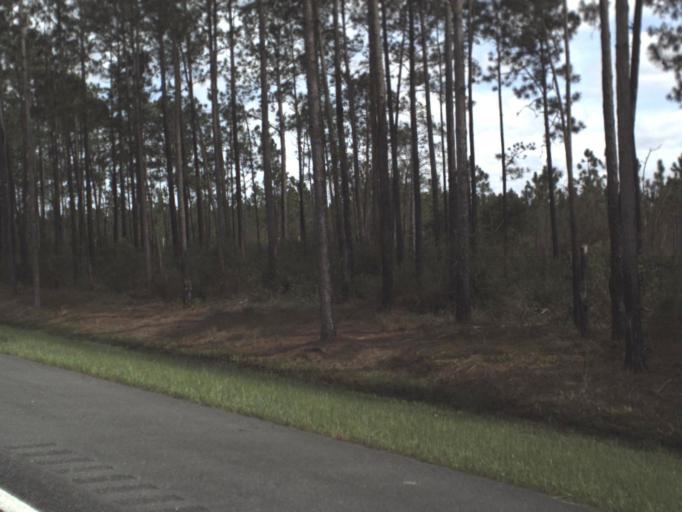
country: US
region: Florida
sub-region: Walton County
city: DeFuniak Springs
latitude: 30.6905
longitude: -86.0367
